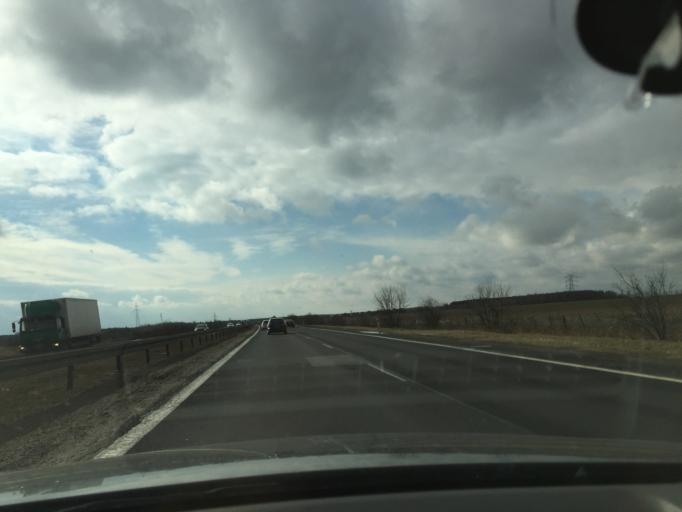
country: PL
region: Lodz Voivodeship
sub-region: Powiat radomszczanski
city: Kamiensk
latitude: 51.1909
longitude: 19.4728
